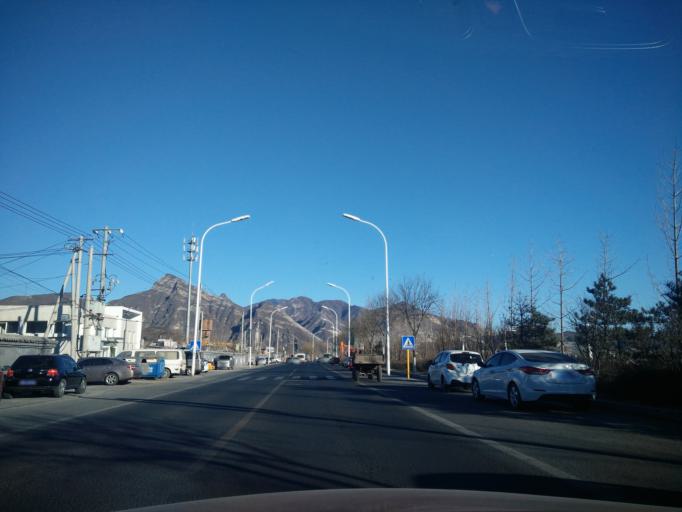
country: CN
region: Beijing
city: Junzhuang
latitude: 39.9839
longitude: 116.0813
